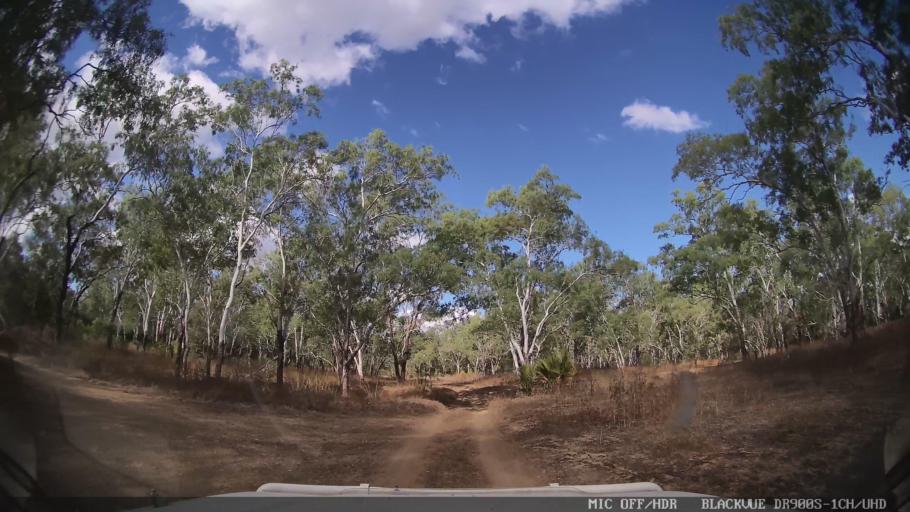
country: AU
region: Queensland
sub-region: Cook
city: Cooktown
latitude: -15.1983
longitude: 144.4231
